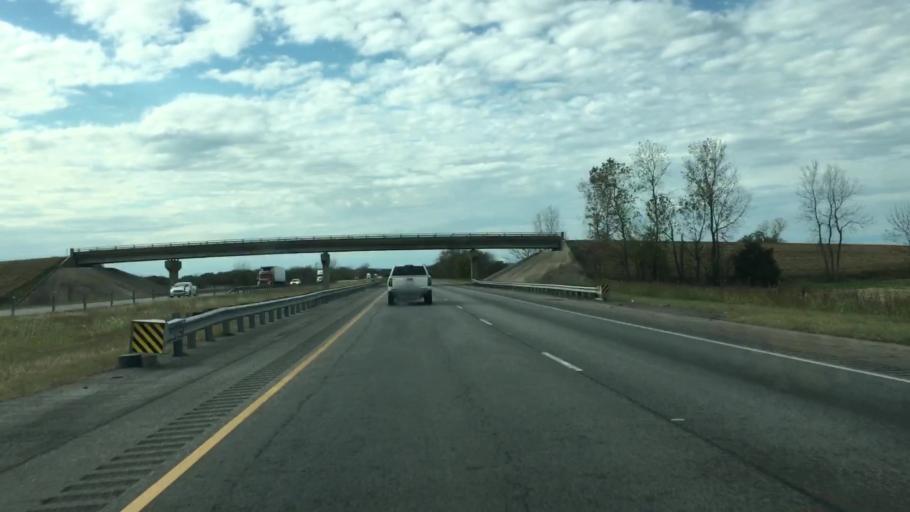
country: US
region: Arkansas
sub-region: Conway County
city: Morrilton
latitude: 35.1909
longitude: -92.7869
